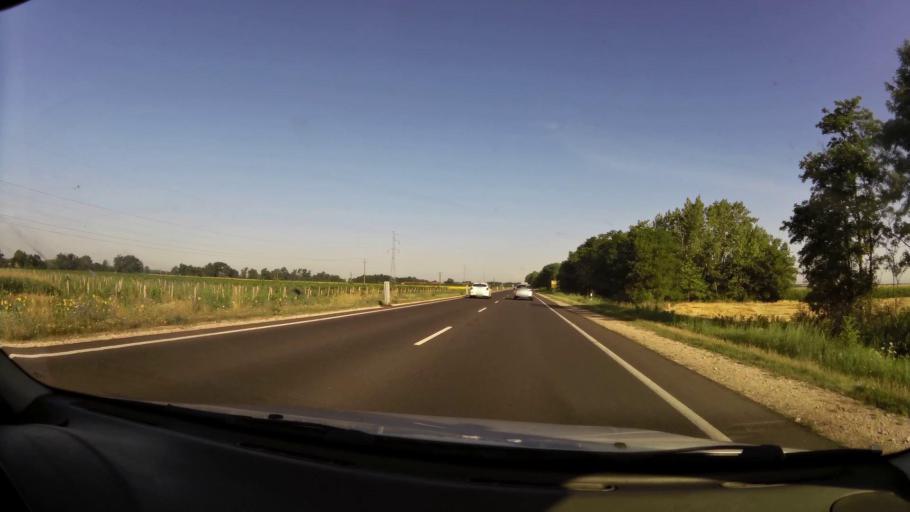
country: HU
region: Pest
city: Cegledbercel
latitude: 47.2167
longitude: 19.7191
